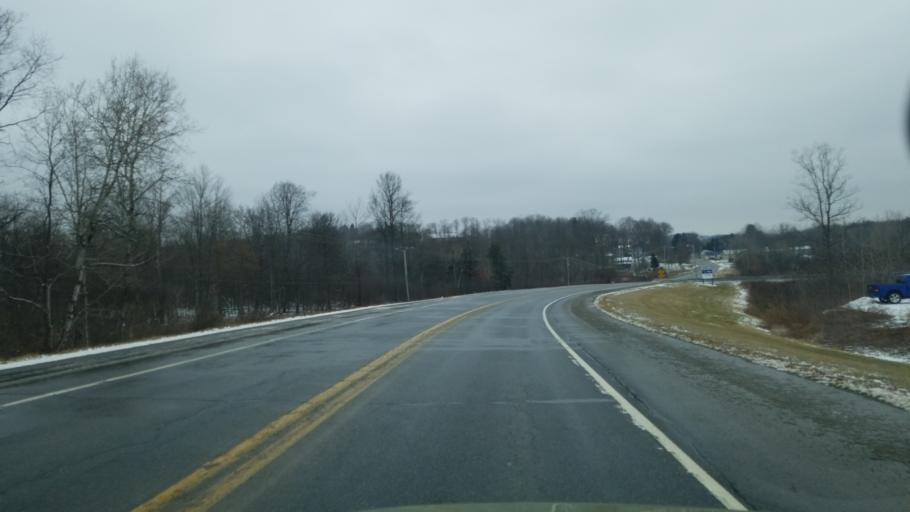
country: US
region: Pennsylvania
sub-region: Jefferson County
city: Falls Creek
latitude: 41.1332
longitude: -78.8109
